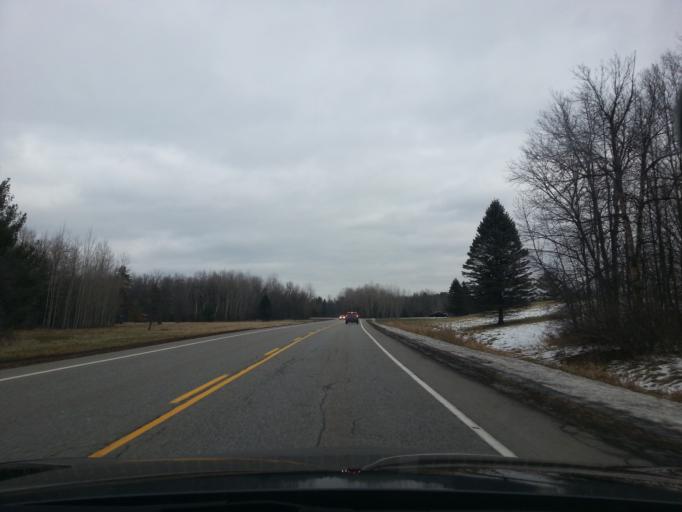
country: CA
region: Quebec
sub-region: Outaouais
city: Gatineau
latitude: 45.4668
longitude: -75.5848
